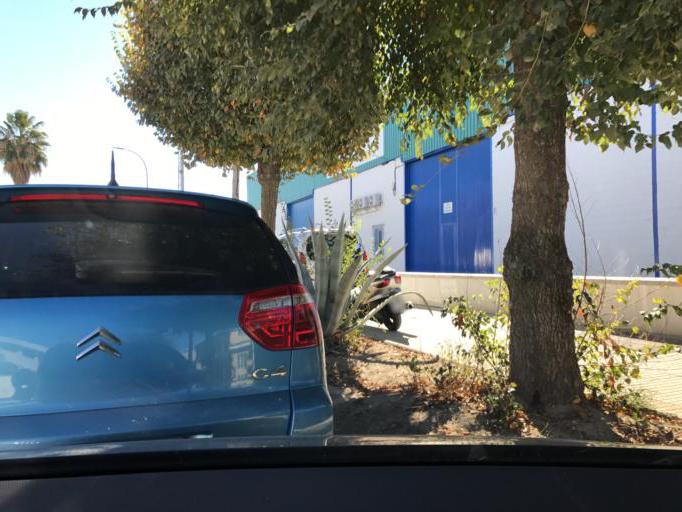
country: ES
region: Andalusia
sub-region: Provincia de Granada
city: Albolote
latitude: 37.2276
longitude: -3.6433
